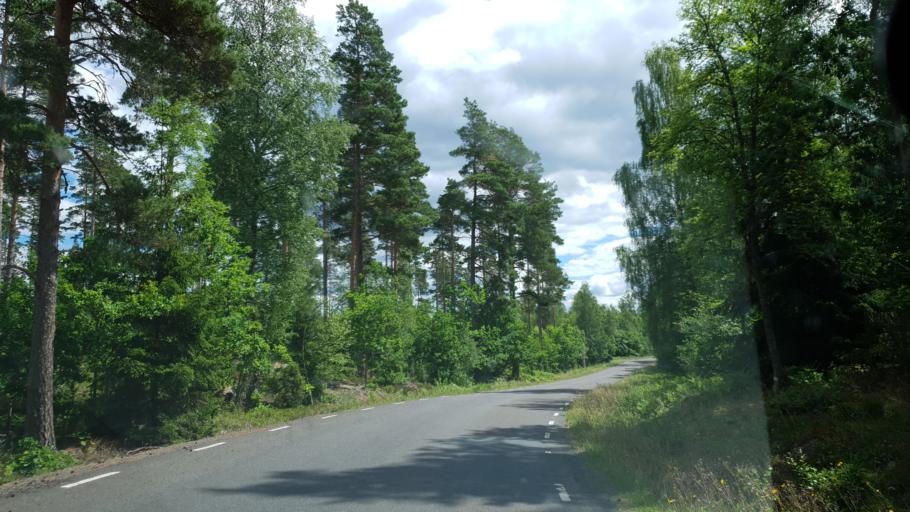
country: SE
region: Kalmar
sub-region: Hultsfreds Kommun
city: Virserum
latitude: 57.1066
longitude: 15.5786
